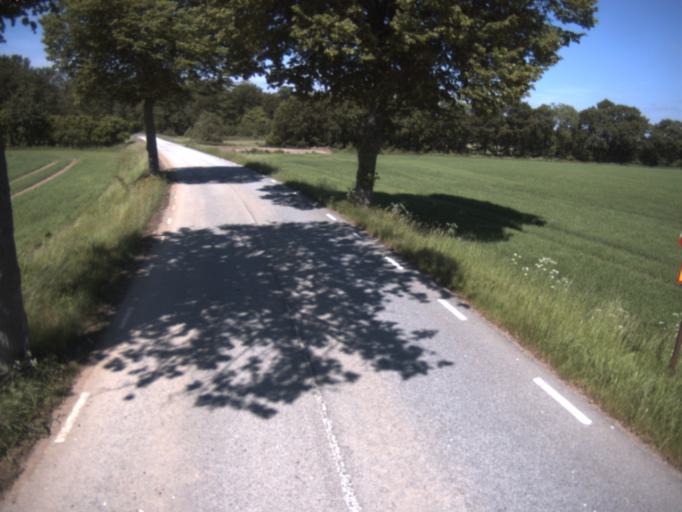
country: SE
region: Skane
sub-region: Helsingborg
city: Odakra
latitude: 56.1125
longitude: 12.6740
